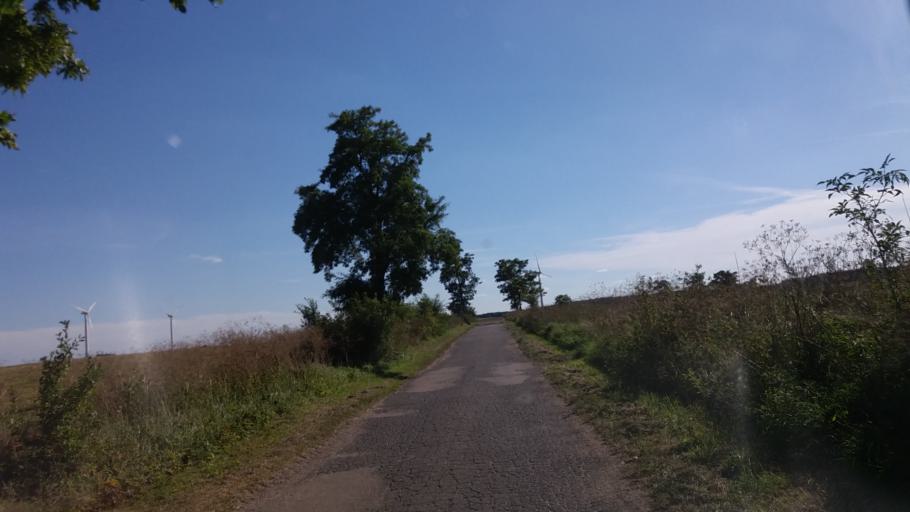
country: PL
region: West Pomeranian Voivodeship
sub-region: Powiat choszczenski
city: Krzecin
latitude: 53.1031
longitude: 15.4918
